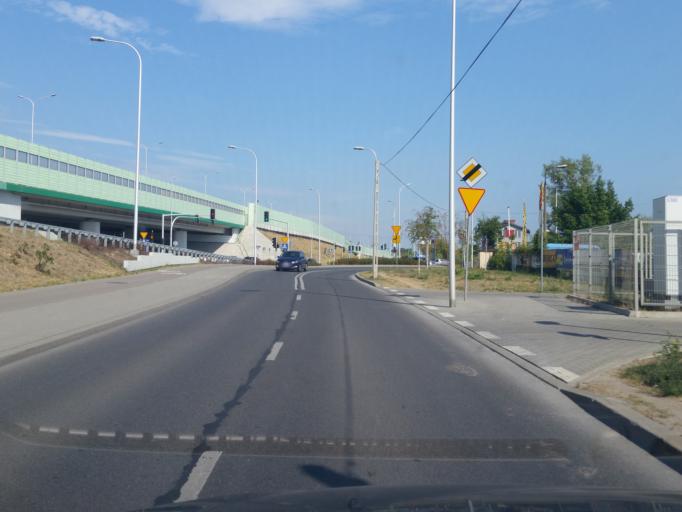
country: PL
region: Masovian Voivodeship
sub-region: Warszawa
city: Bialoleka
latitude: 52.3120
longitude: 20.9649
